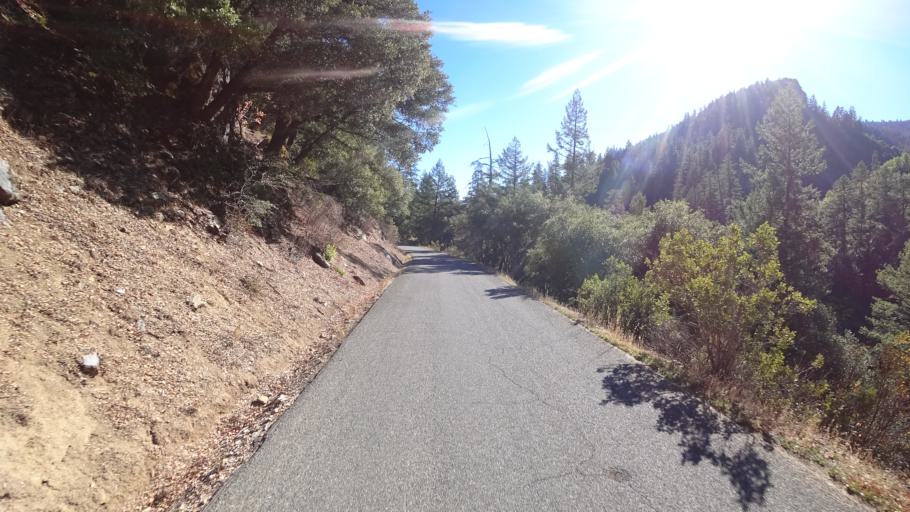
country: US
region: California
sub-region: Humboldt County
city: Willow Creek
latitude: 41.1457
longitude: -123.2001
